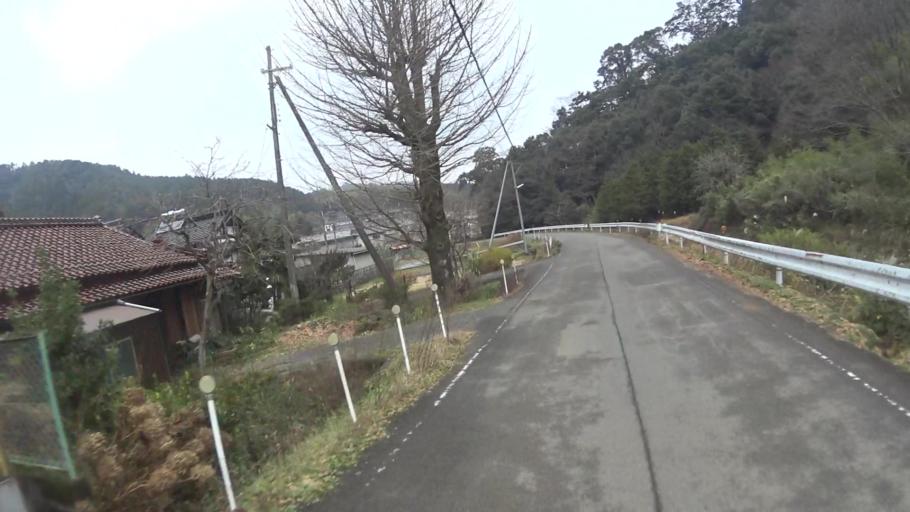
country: JP
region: Kyoto
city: Maizuru
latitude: 35.4265
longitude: 135.2977
